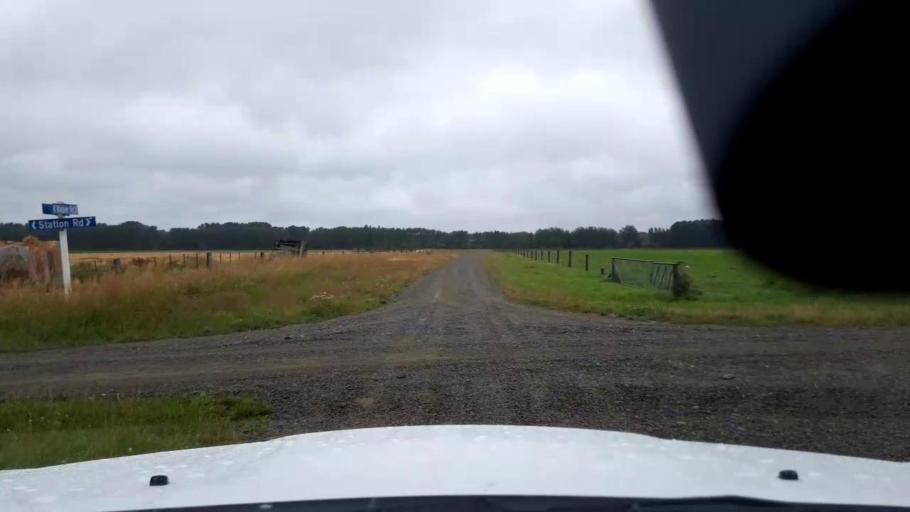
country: NZ
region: Canterbury
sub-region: Timaru District
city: Pleasant Point
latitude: -44.2533
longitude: 171.2001
